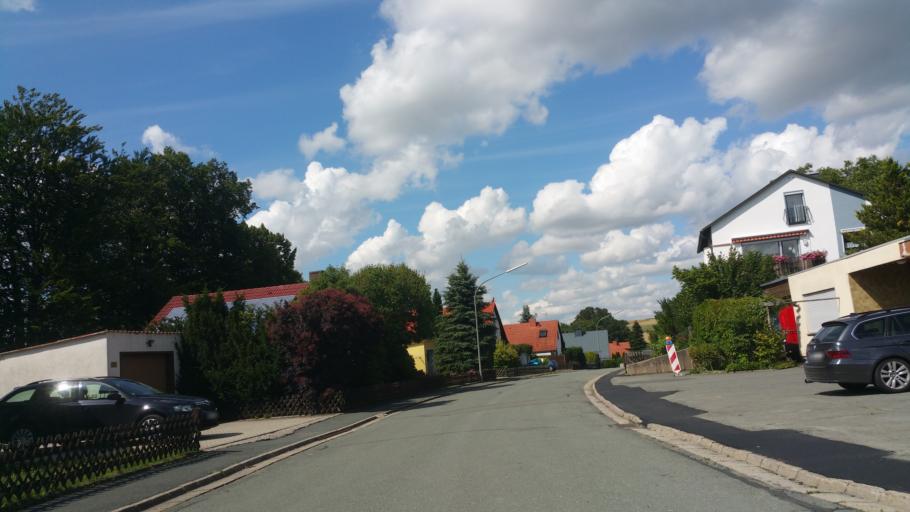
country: DE
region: Bavaria
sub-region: Upper Franconia
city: Oberkotzau
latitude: 50.2604
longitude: 11.9378
